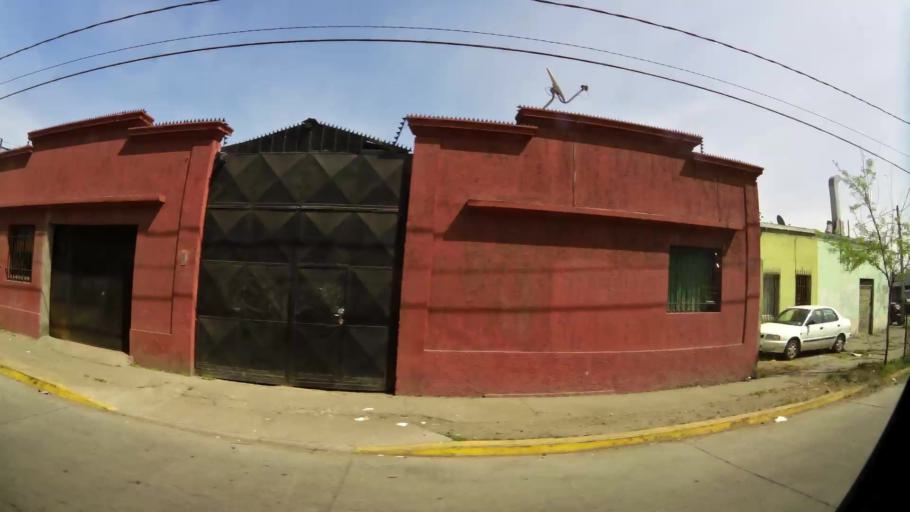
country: CL
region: Santiago Metropolitan
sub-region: Provincia de Santiago
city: Lo Prado
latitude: -33.4242
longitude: -70.7218
